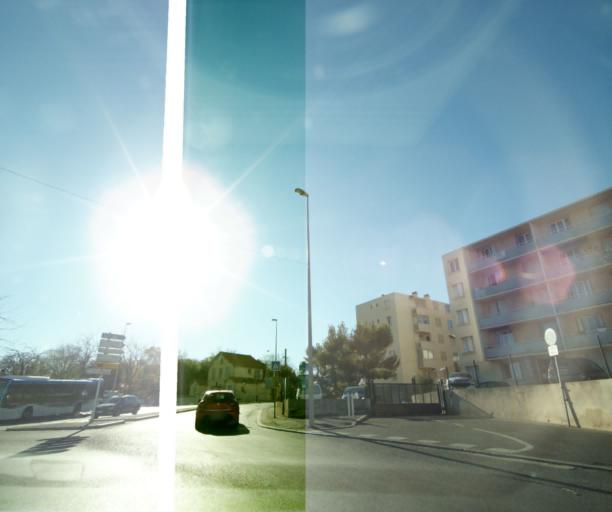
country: FR
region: Provence-Alpes-Cote d'Azur
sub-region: Departement des Bouches-du-Rhone
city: Marseille 15
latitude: 43.3737
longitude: 5.3546
